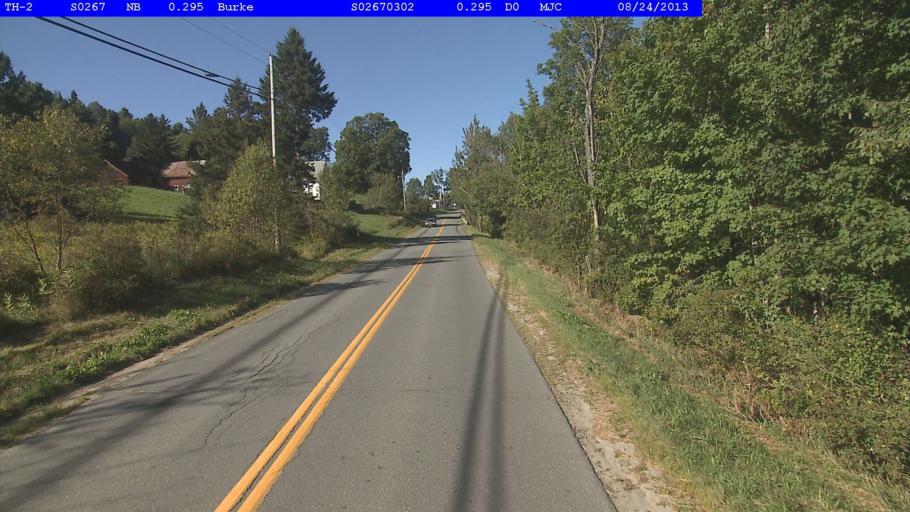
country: US
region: Vermont
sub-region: Caledonia County
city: Lyndonville
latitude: 44.5914
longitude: -71.9453
